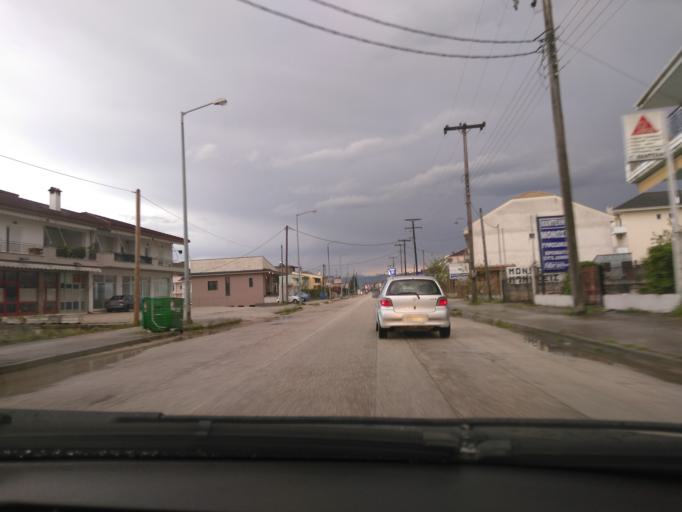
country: GR
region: Epirus
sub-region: Nomos Ioanninon
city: Anatoli
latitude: 39.6355
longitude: 20.8723
